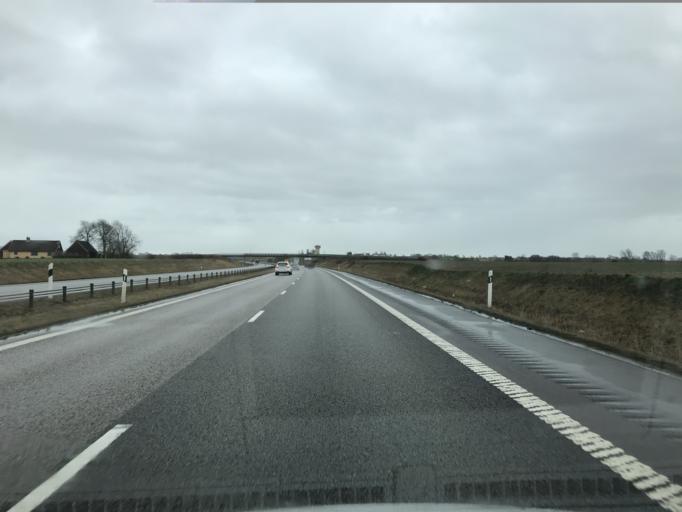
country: SE
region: Skane
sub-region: Angelholms Kommun
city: AEngelholm
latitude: 56.2742
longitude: 12.8948
